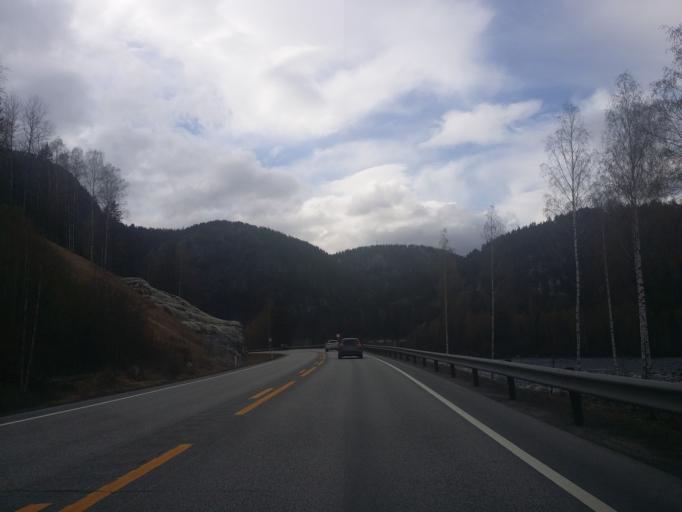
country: NO
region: Buskerud
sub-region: Nes
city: Nesbyen
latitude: 60.4696
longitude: 9.2405
